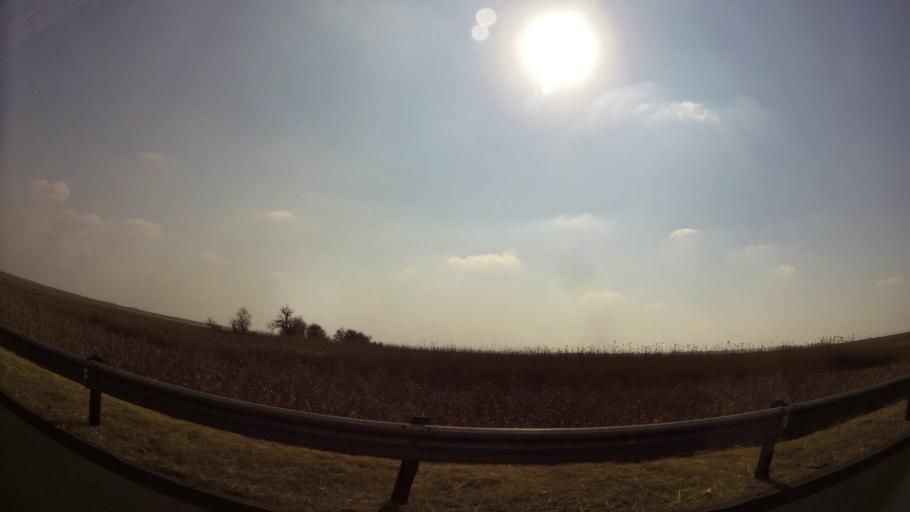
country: ZA
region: Gauteng
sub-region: Ekurhuleni Metropolitan Municipality
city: Springs
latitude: -26.1651
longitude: 28.4612
